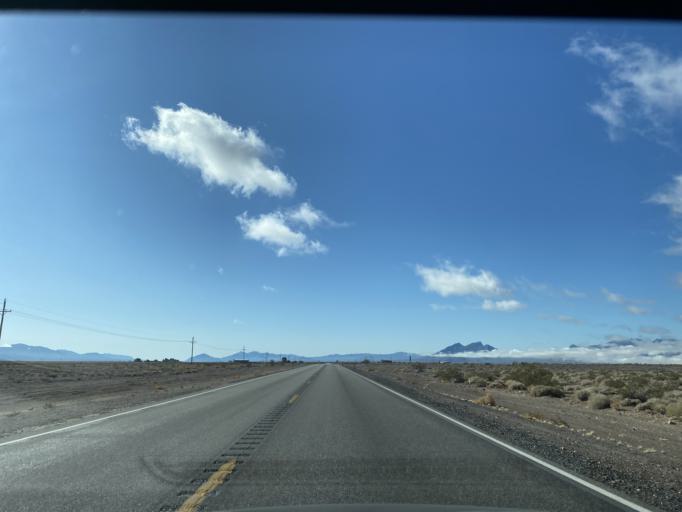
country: US
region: Nevada
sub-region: Nye County
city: Beatty
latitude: 36.5363
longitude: -116.4181
